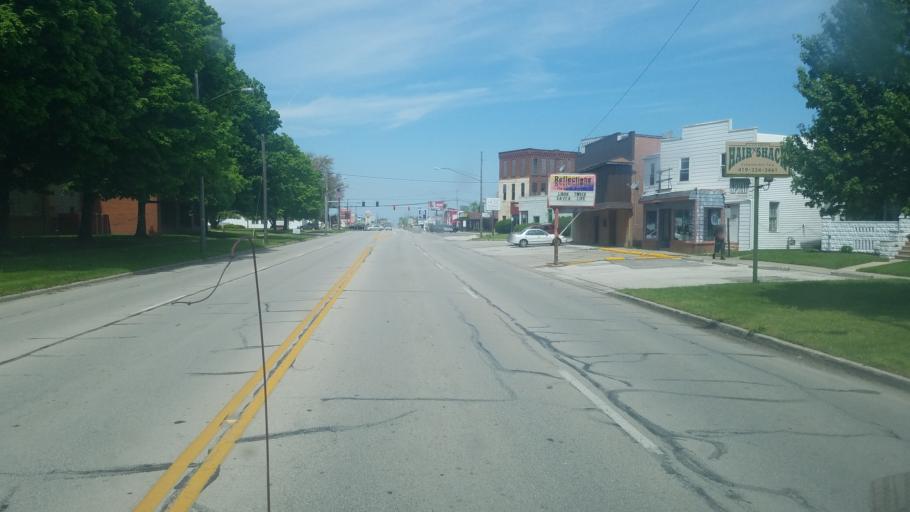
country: US
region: Ohio
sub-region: Sandusky County
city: Fremont
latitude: 41.3542
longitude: -83.1303
